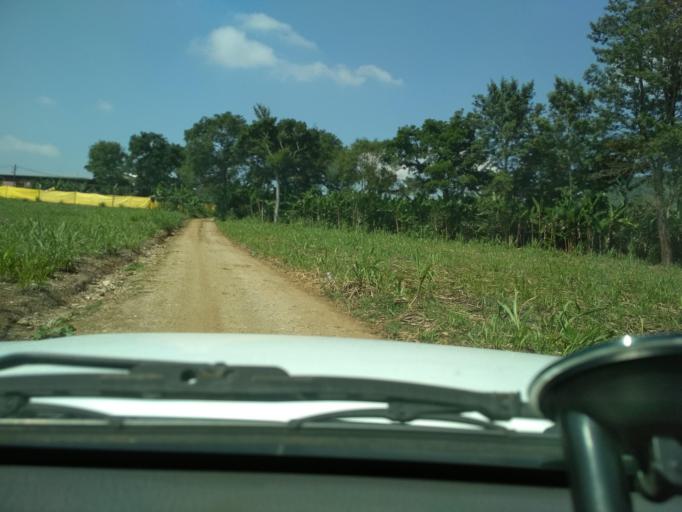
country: MX
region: Veracruz
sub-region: Fortin
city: Santa Lucia Potrerillo
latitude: 18.9817
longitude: -97.0181
